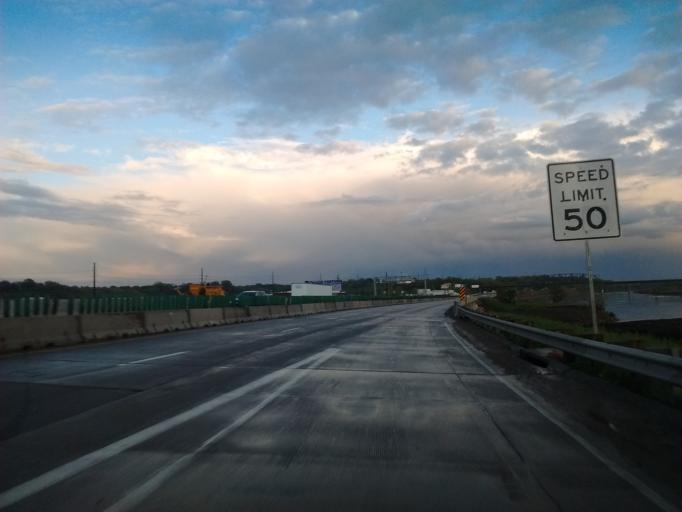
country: US
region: Iowa
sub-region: Woodbury County
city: Sioux City
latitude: 42.4847
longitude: -96.3927
